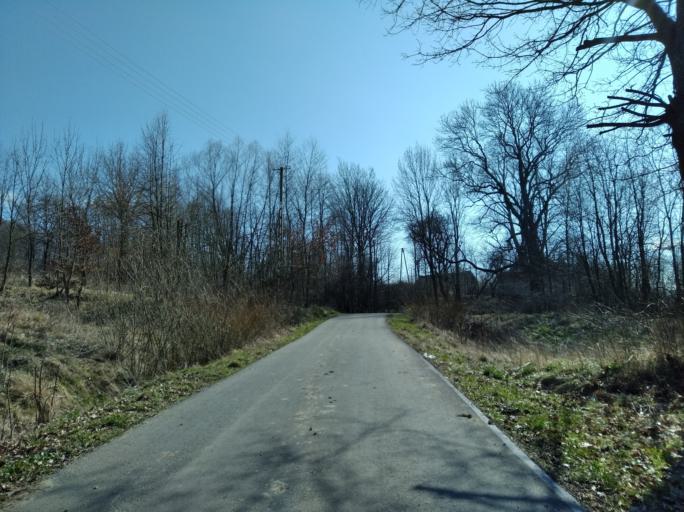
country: PL
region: Subcarpathian Voivodeship
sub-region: Powiat strzyzowski
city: Wysoka Strzyzowska
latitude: 49.8371
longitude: 21.7439
